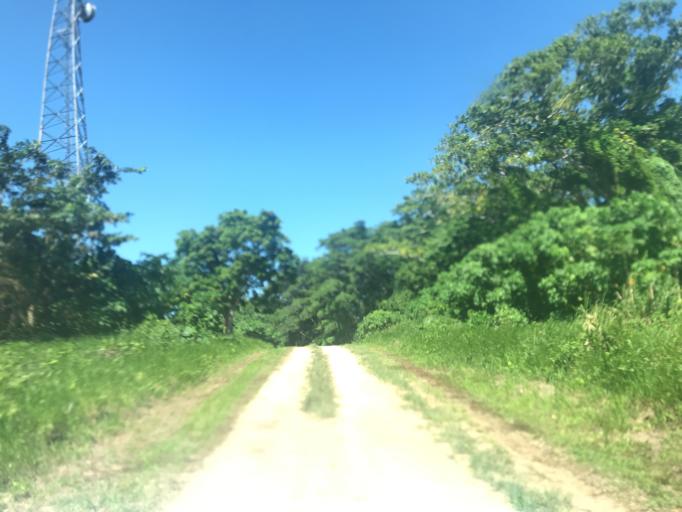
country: VU
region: Sanma
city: Luganville
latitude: -15.6401
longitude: 166.8094
